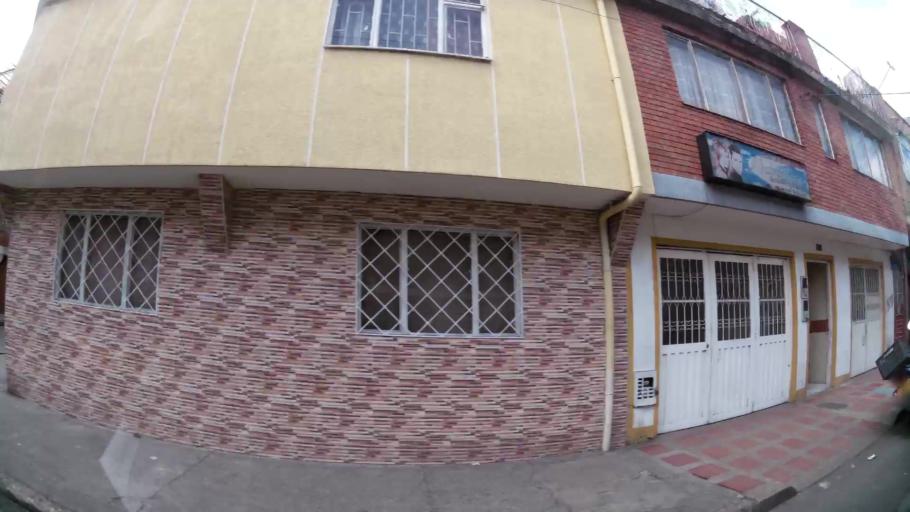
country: CO
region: Bogota D.C.
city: Bogota
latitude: 4.6956
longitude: -74.1140
